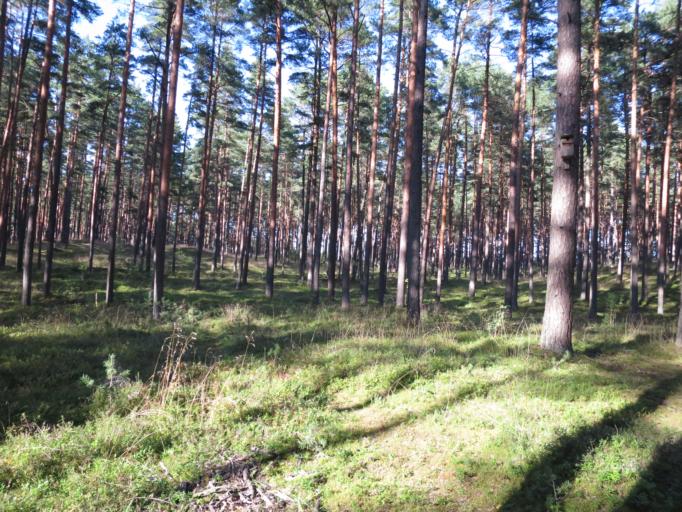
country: LV
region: Riga
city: Jaunciems
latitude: 57.0777
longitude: 24.1999
